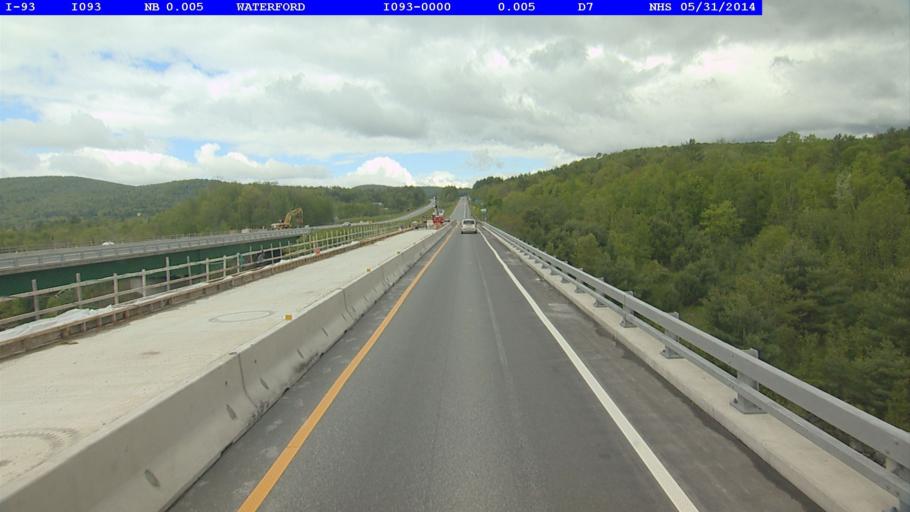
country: US
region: New Hampshire
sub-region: Grafton County
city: Littleton
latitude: 44.3429
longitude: -71.8907
